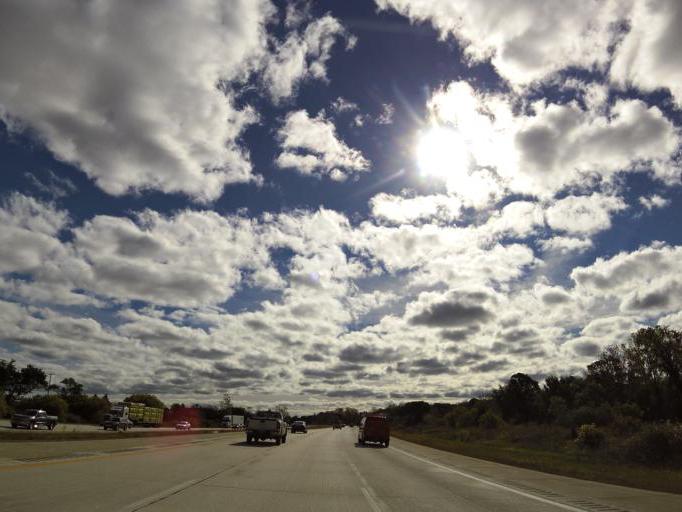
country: US
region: Michigan
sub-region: Genesee County
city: Burton
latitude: 43.0189
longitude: -83.5784
